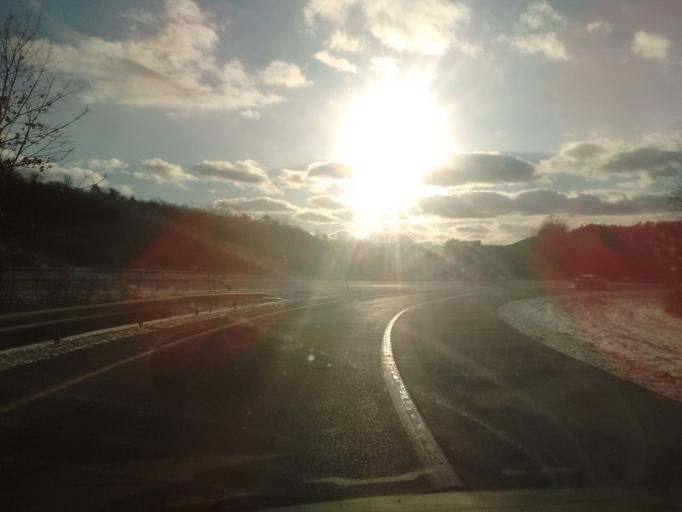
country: US
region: New York
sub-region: Orange County
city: Port Jervis
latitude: 41.3540
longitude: -74.6788
